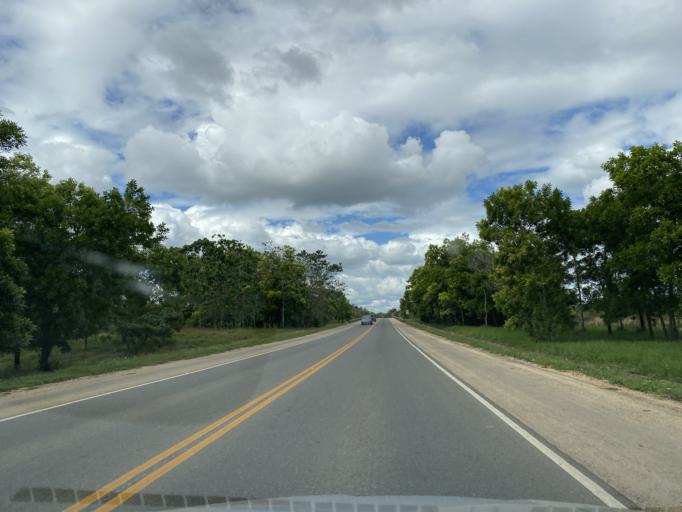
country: DO
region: Santo Domingo
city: Guerra
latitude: 18.5422
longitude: -69.7587
